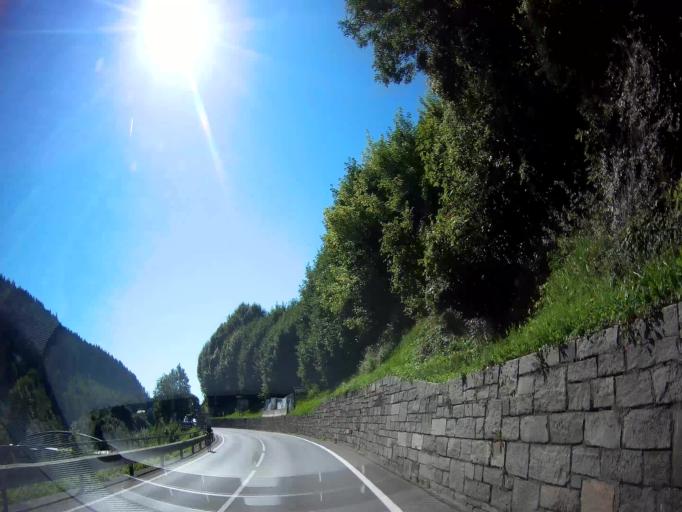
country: AT
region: Carinthia
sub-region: Politischer Bezirk Spittal an der Drau
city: Spittal an der Drau
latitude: 46.8027
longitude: 13.4959
